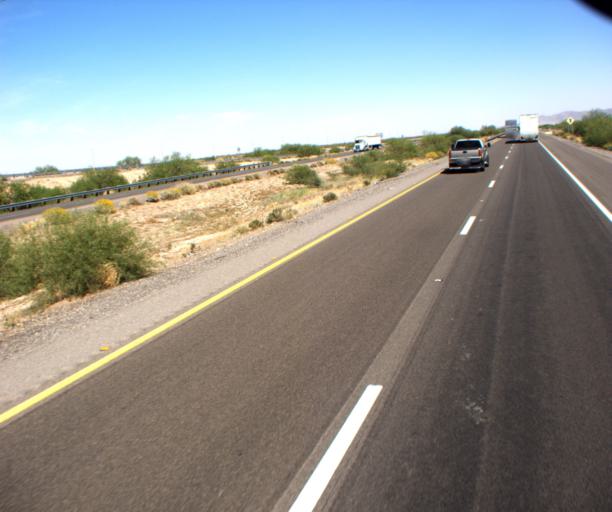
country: US
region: Arizona
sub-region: Pinal County
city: Casa Grande
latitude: 32.8279
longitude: -111.8604
